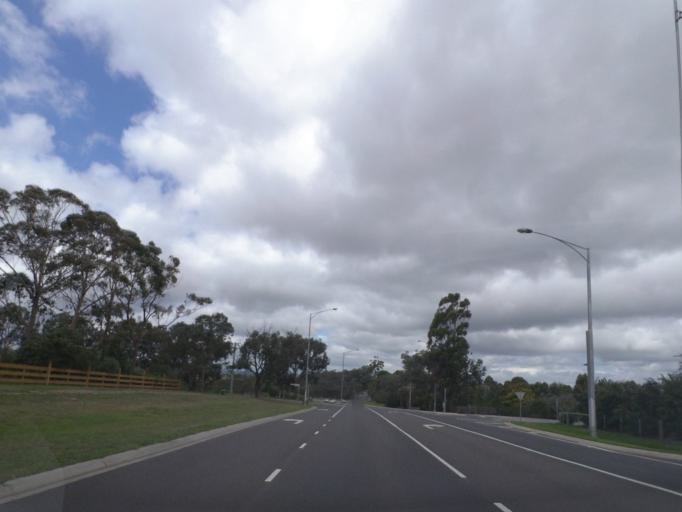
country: AU
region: Victoria
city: Plenty
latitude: -37.6765
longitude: 145.1316
